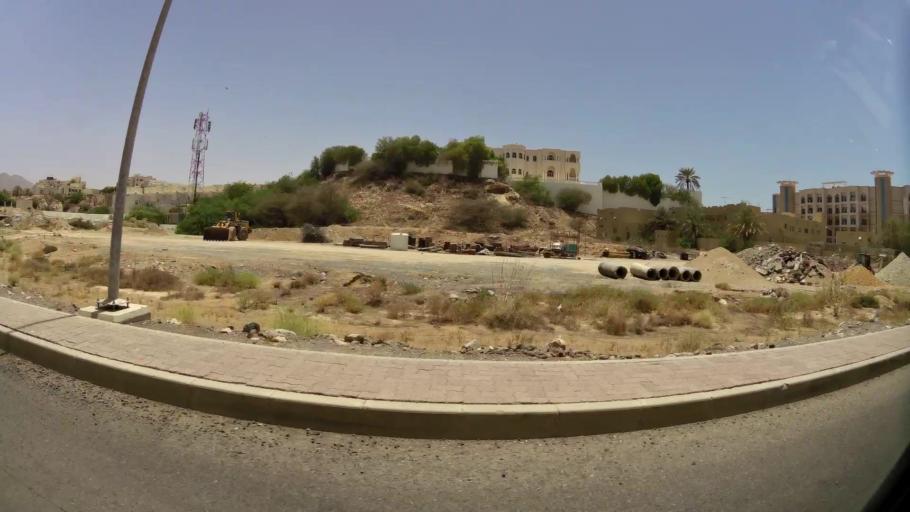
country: OM
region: Muhafazat Masqat
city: Bawshar
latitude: 23.6095
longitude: 58.4781
